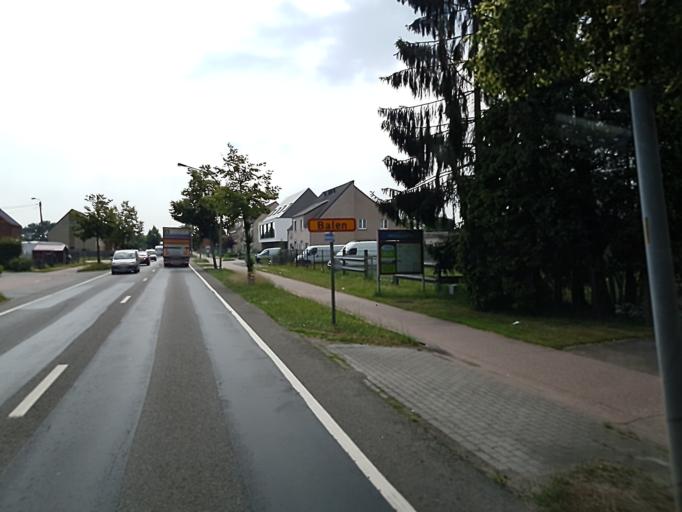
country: BE
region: Flanders
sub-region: Provincie Antwerpen
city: Mol
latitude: 51.1761
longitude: 5.1324
